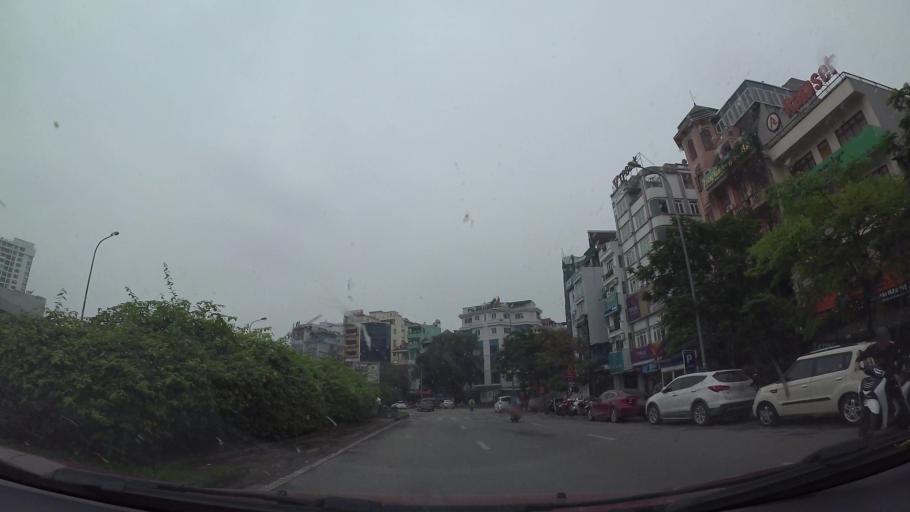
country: VN
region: Ha Noi
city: Dong Da
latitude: 21.0164
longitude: 105.8227
